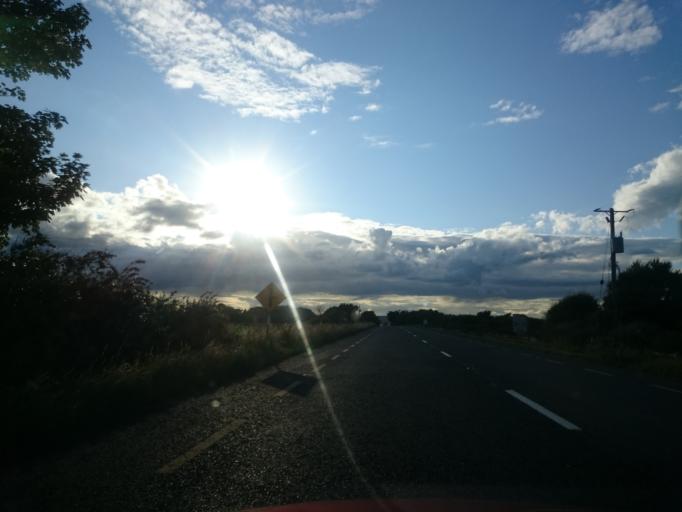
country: IE
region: Leinster
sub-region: Loch Garman
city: Rosslare
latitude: 52.2522
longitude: -6.4146
